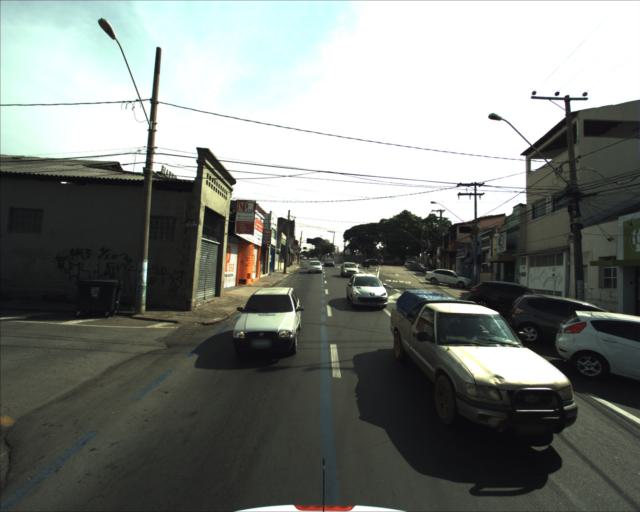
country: BR
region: Sao Paulo
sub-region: Sorocaba
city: Sorocaba
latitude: -23.4929
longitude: -47.4596
